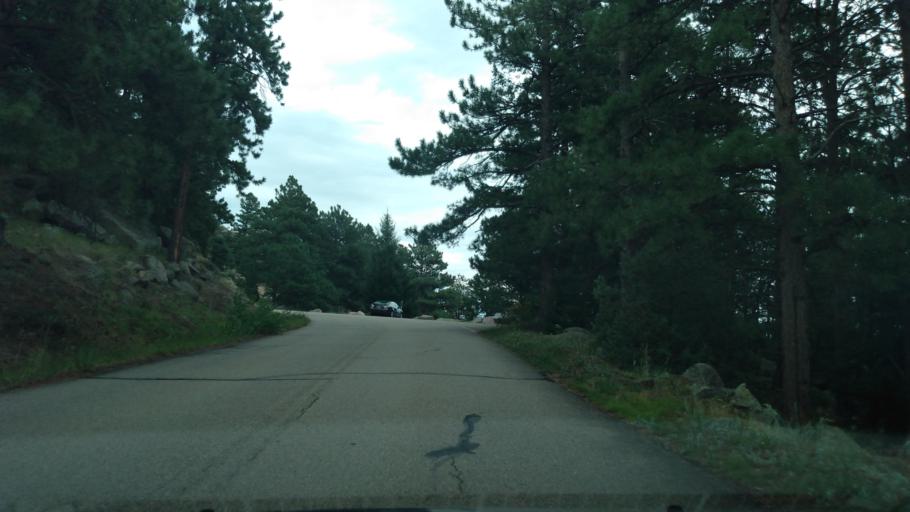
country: US
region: Colorado
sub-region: Boulder County
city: Boulder
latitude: 39.9983
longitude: -105.3084
